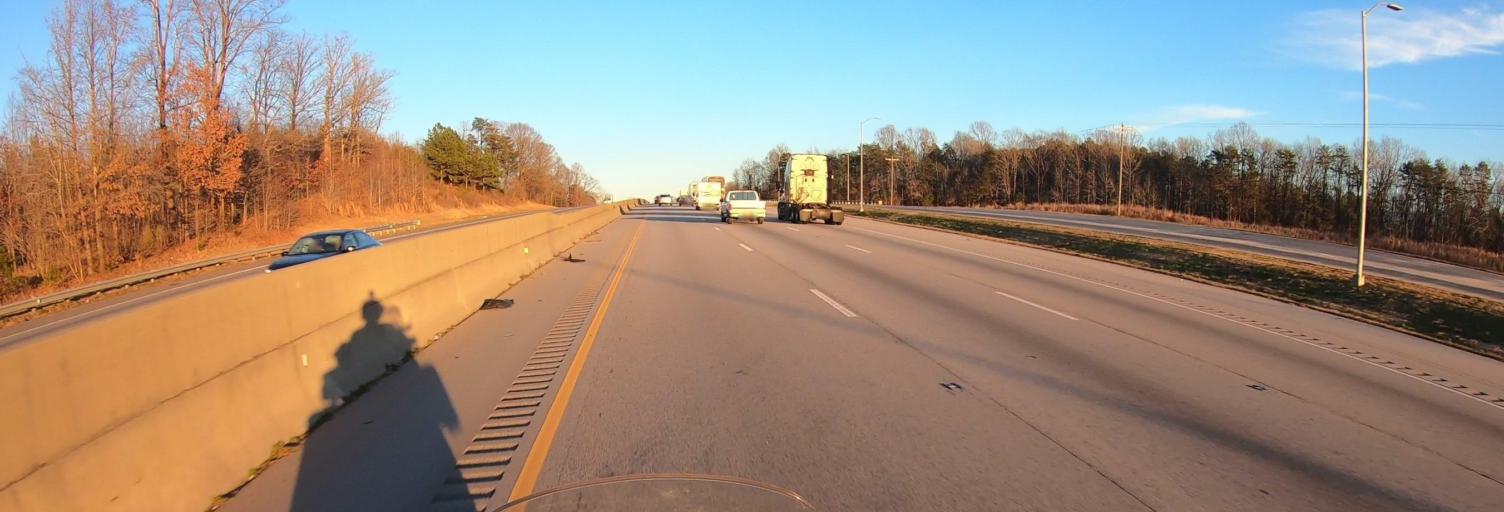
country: US
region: North Carolina
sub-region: Gaston County
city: Bessemer City
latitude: 35.2600
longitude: -81.2756
